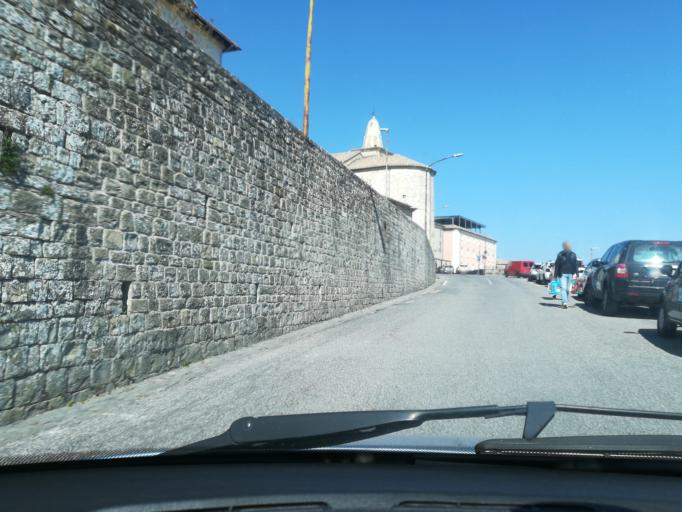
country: IT
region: The Marches
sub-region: Provincia di Macerata
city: Cingoli
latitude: 43.3751
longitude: 13.2179
